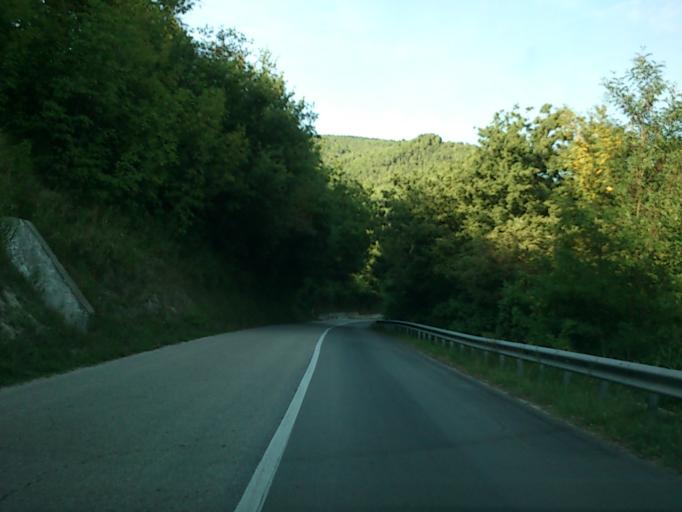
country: IT
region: The Marches
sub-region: Provincia di Pesaro e Urbino
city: Fossombrone
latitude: 43.6772
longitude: 12.7594
